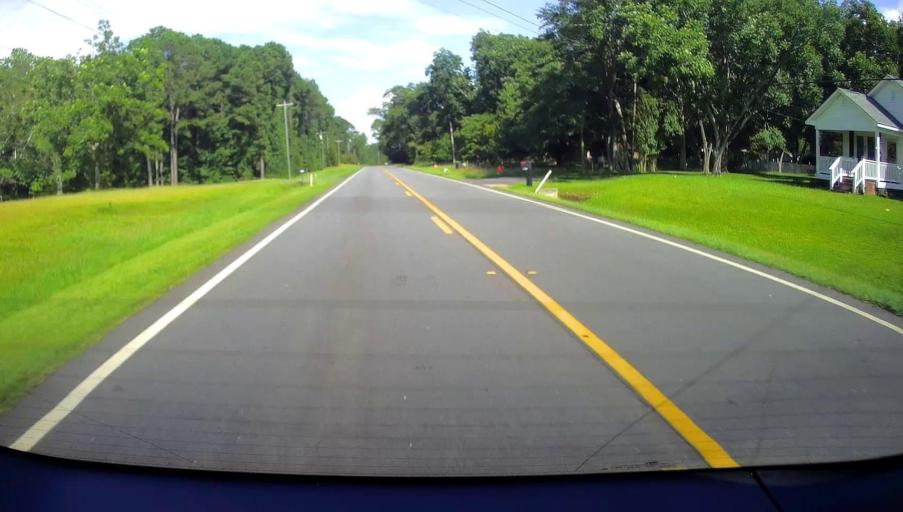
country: US
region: Georgia
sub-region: Upson County
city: Hannahs Mill
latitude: 32.8978
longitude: -84.4009
